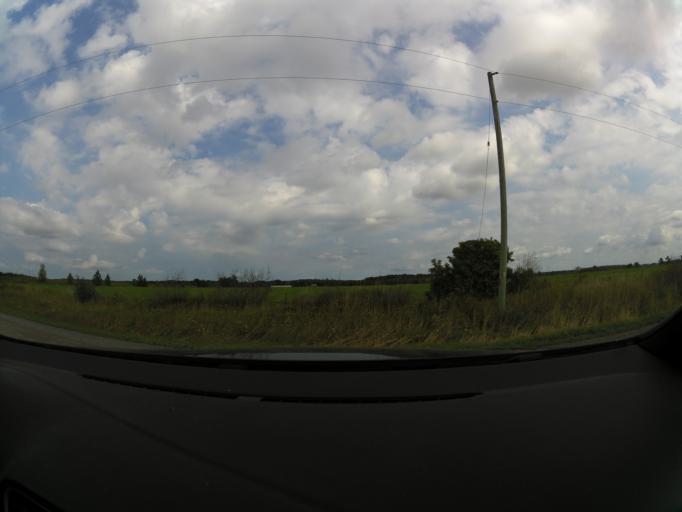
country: CA
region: Ontario
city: Arnprior
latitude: 45.3874
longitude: -76.2532
